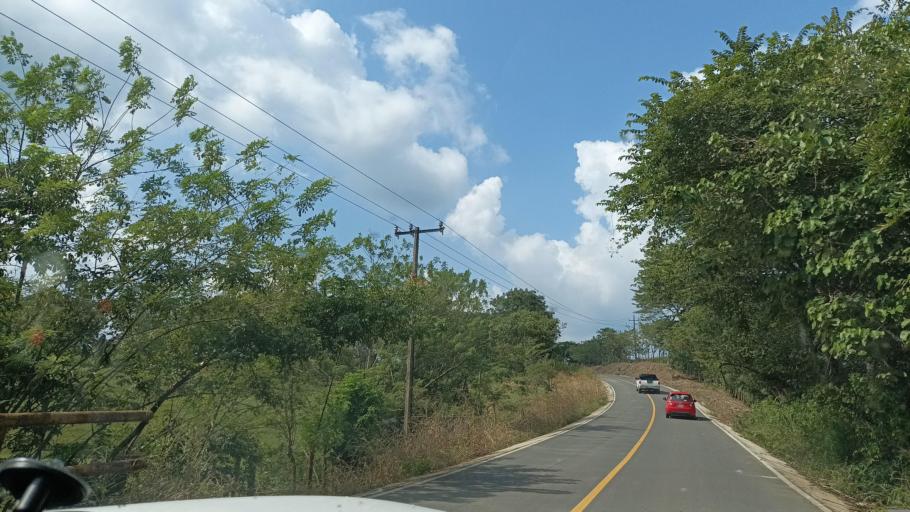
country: MX
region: Veracruz
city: Las Choapas
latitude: 17.7415
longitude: -94.1089
